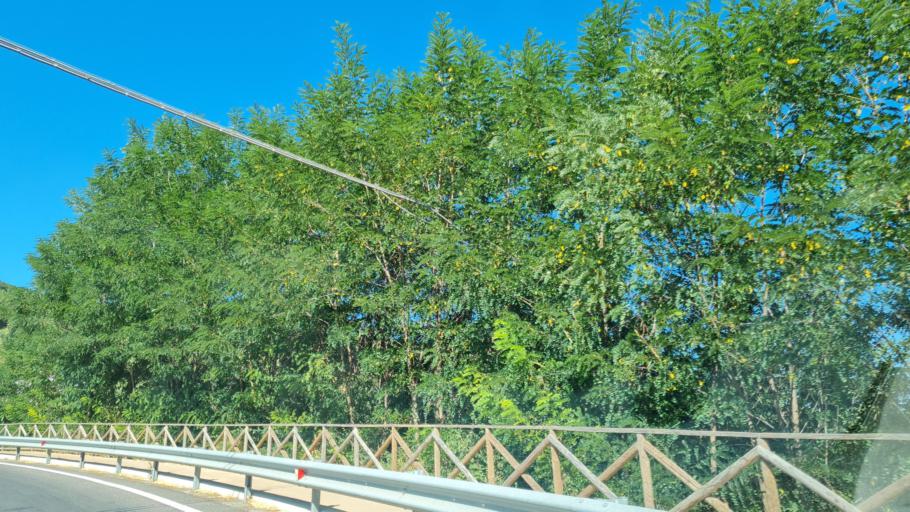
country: IT
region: Tuscany
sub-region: Provincia di Siena
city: Sant'Albino
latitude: 43.0655
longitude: 11.8136
